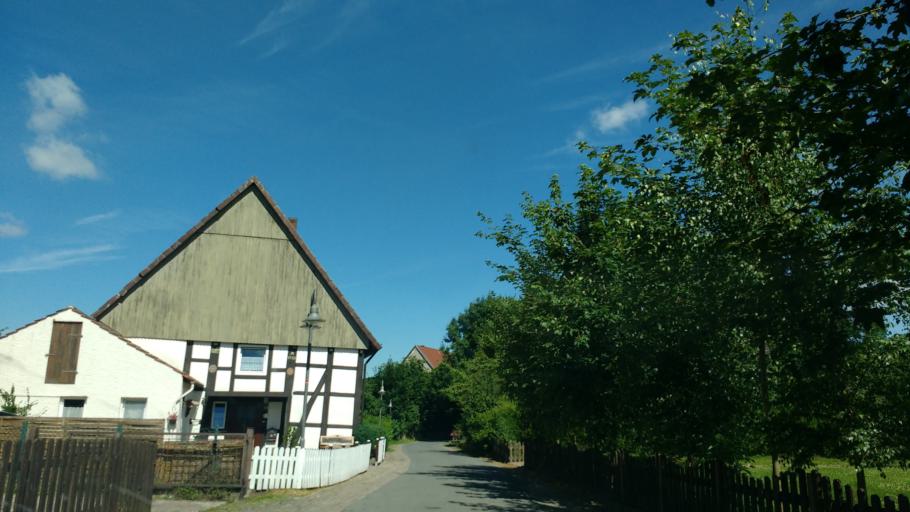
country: DE
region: North Rhine-Westphalia
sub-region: Regierungsbezirk Detmold
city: Dorentrup
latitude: 52.0214
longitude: 9.0565
